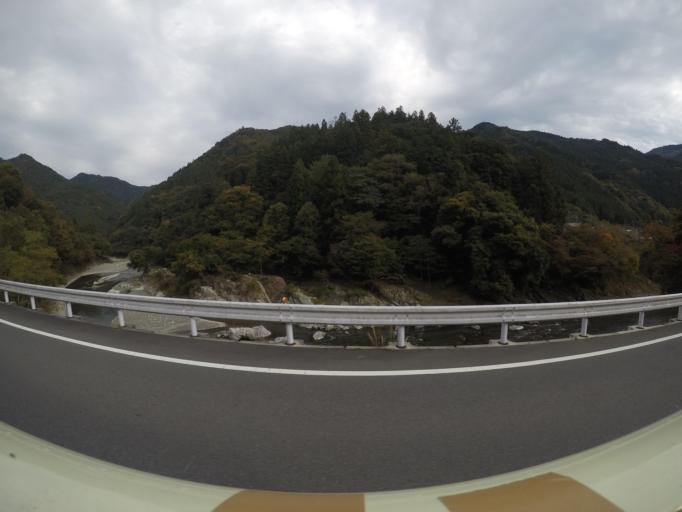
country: JP
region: Gunma
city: Yoshii
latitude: 36.1248
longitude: 138.9409
